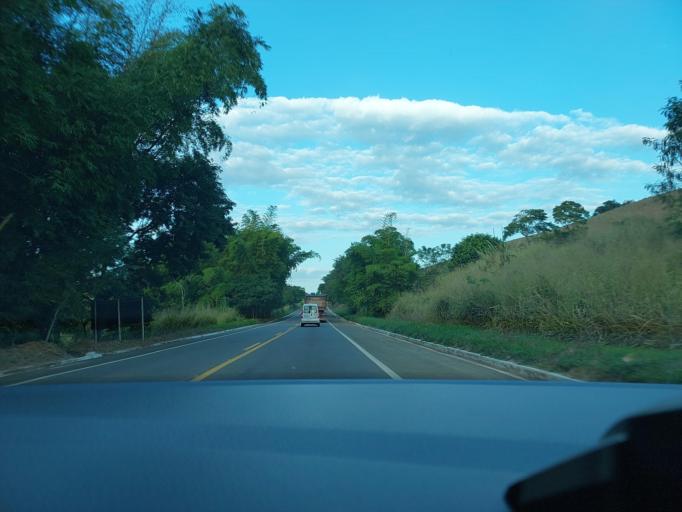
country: BR
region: Minas Gerais
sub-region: Muriae
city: Muriae
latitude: -21.1362
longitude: -42.1831
